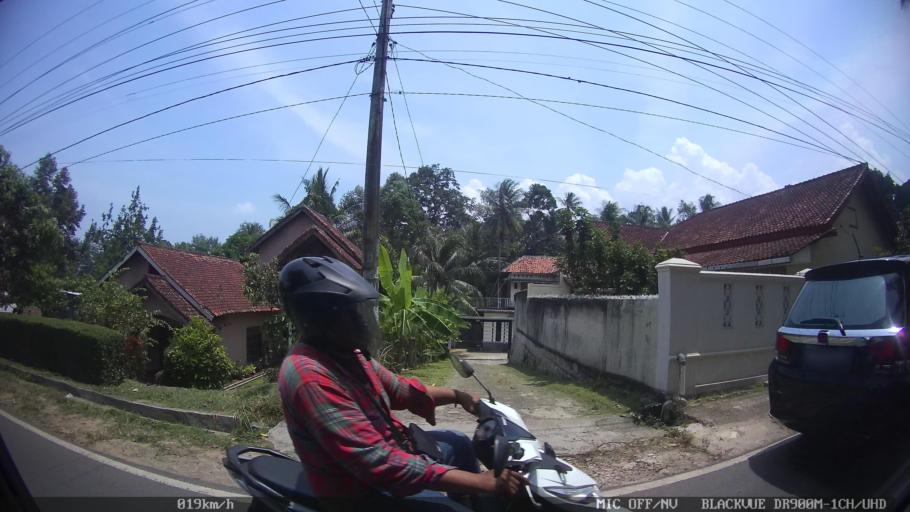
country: ID
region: Lampung
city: Bandarlampung
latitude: -5.4425
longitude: 105.2426
